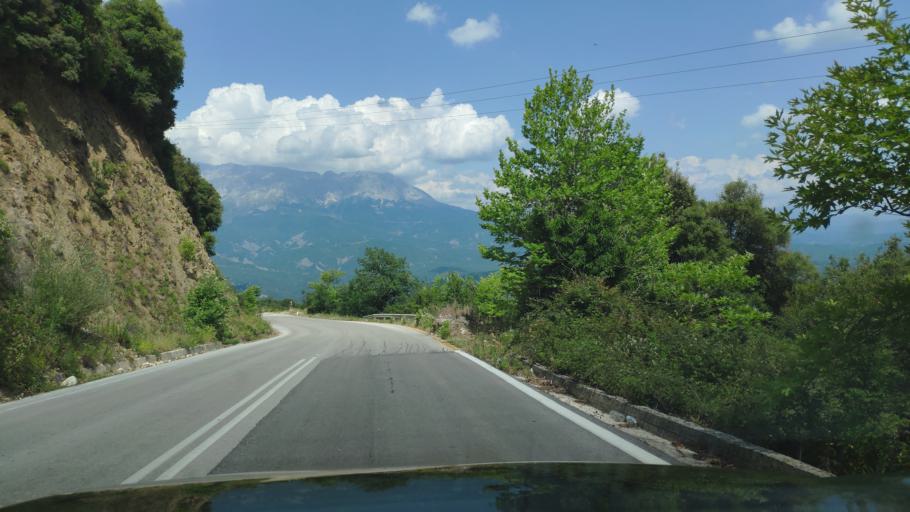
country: GR
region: Epirus
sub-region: Nomos Artas
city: Agios Dimitrios
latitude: 39.3482
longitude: 21.0121
